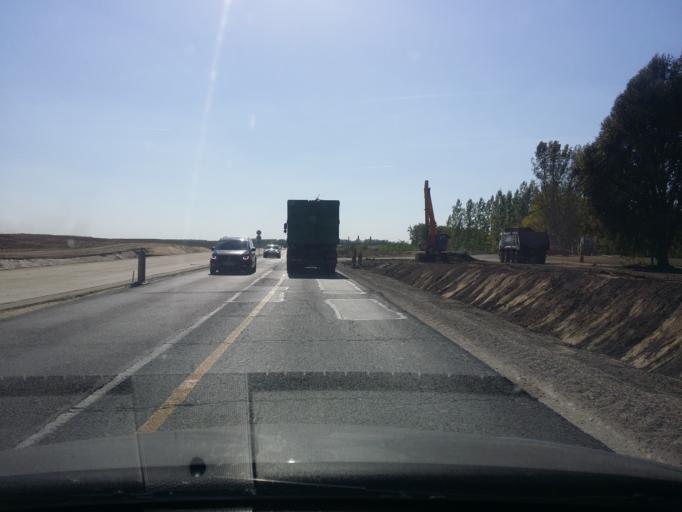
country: HU
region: Bacs-Kiskun
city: Kecskemet
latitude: 46.8682
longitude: 19.6832
